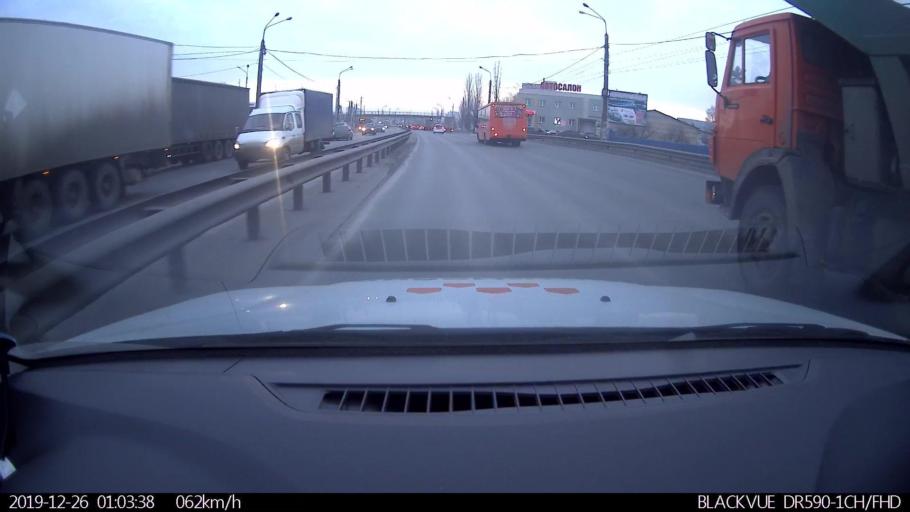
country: RU
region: Nizjnij Novgorod
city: Nizhniy Novgorod
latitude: 56.2834
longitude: 43.8923
